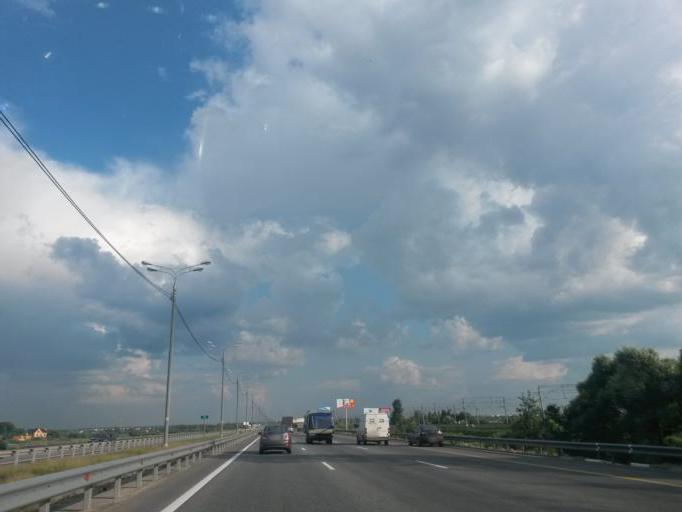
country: RU
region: Moskovskaya
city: Yam
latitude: 55.5044
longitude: 37.7232
